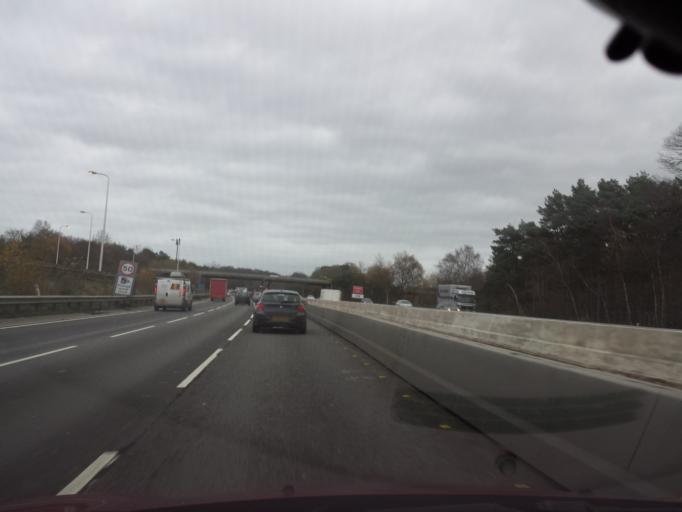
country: GB
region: England
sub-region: Surrey
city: Chobham
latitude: 51.3798
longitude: -0.5928
